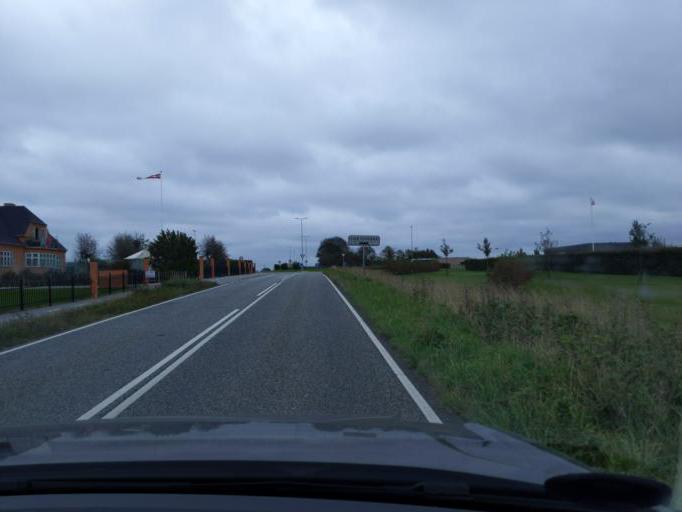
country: DK
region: Central Jutland
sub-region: Randers Kommune
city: Randers
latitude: 56.4609
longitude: 9.9540
